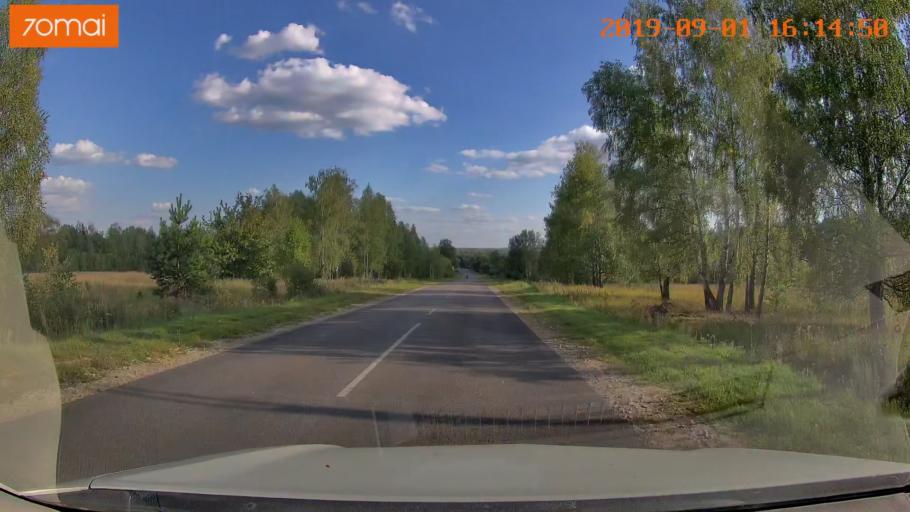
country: RU
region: Kaluga
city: Maloyaroslavets
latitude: 54.9282
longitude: 36.4724
